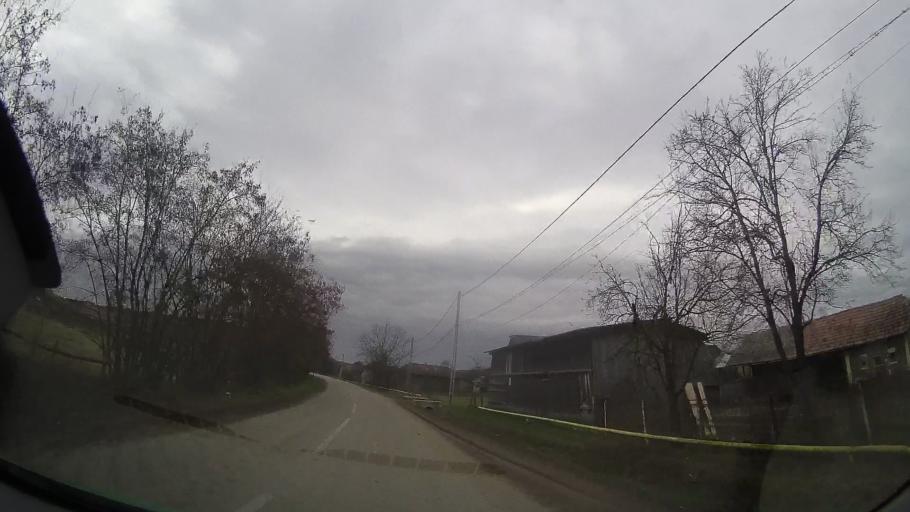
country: RO
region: Bistrita-Nasaud
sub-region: Comuna Milas
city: Milas
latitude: 46.8083
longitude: 24.4277
